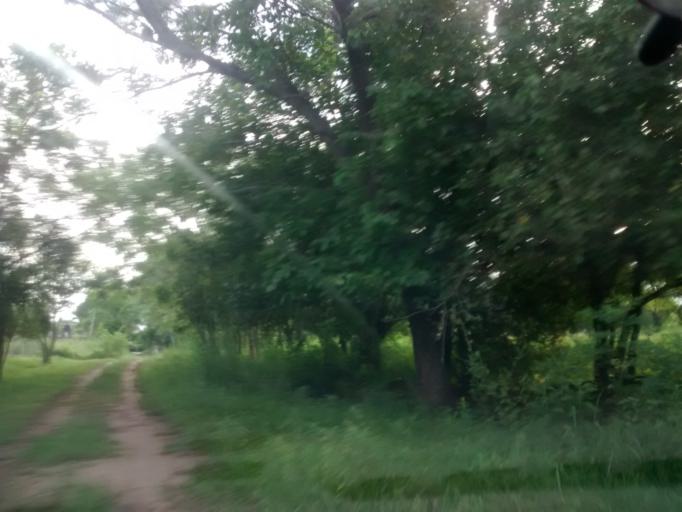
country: AR
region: Chaco
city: Fontana
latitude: -27.4213
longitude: -59.0049
